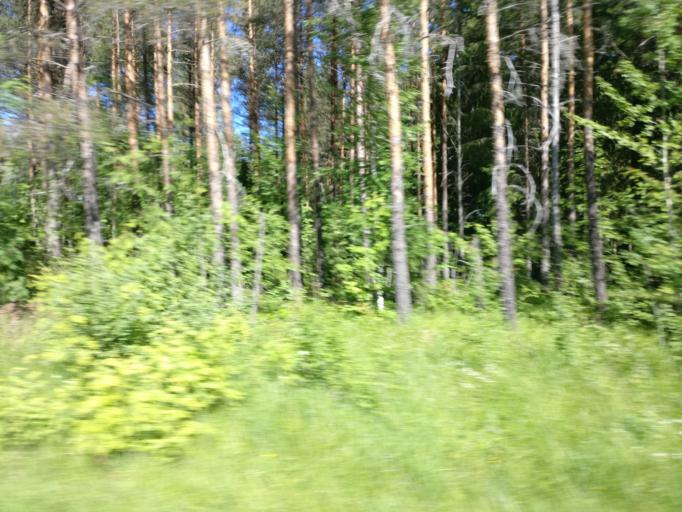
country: FI
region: Southern Savonia
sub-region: Savonlinna
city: Rantasalmi
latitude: 62.0934
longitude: 28.2793
